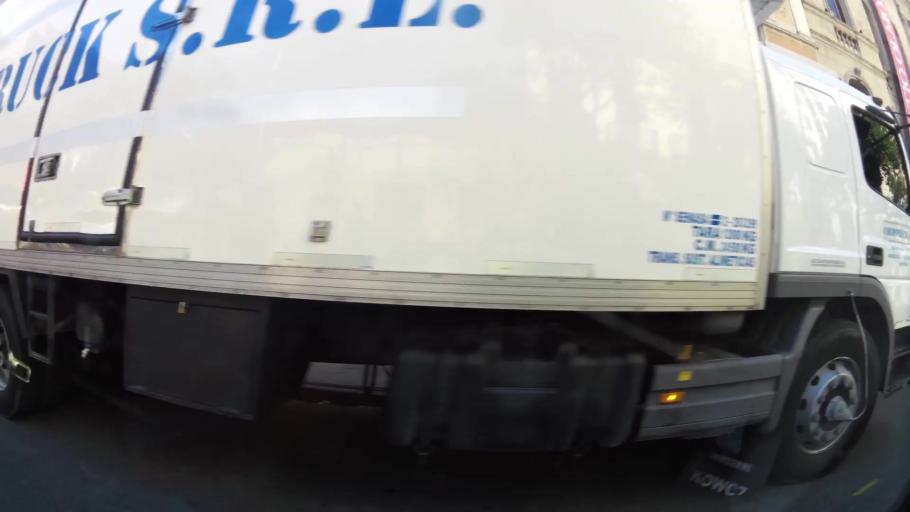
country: AR
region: Cordoba
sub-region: Departamento de Capital
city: Cordoba
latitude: -31.4194
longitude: -64.1884
